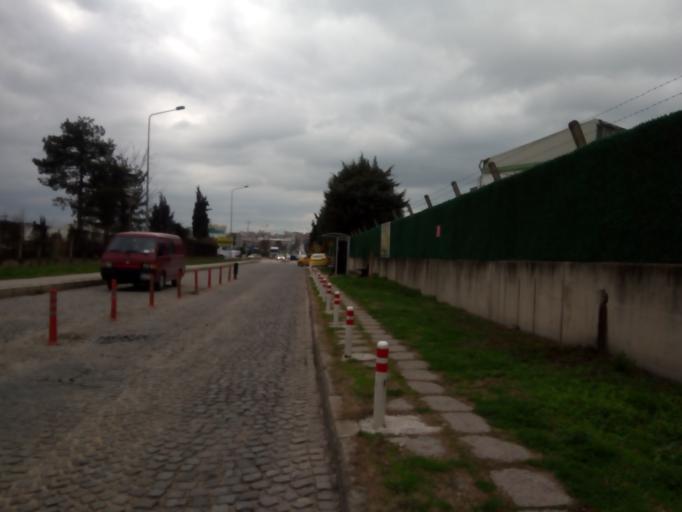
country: TR
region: Bursa
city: Niluefer
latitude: 40.2499
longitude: 28.9567
